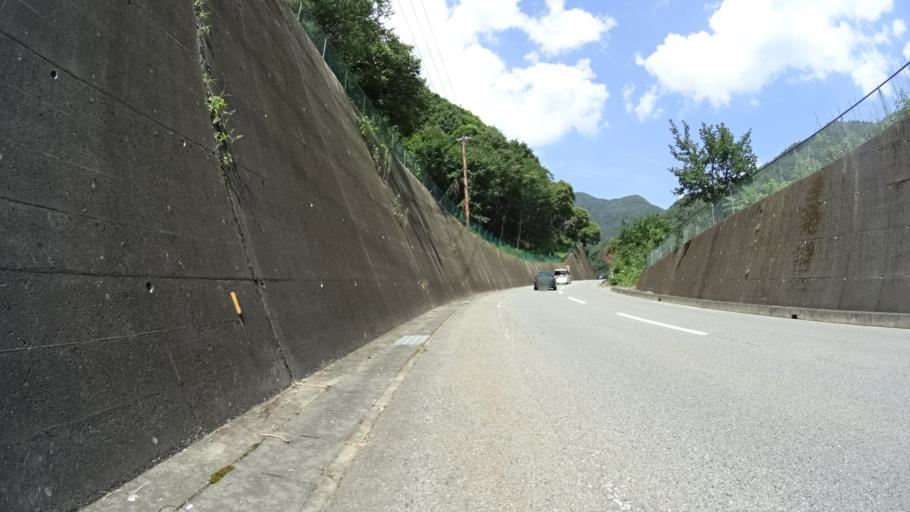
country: JP
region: Gunma
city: Tomioka
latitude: 36.0811
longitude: 138.7742
